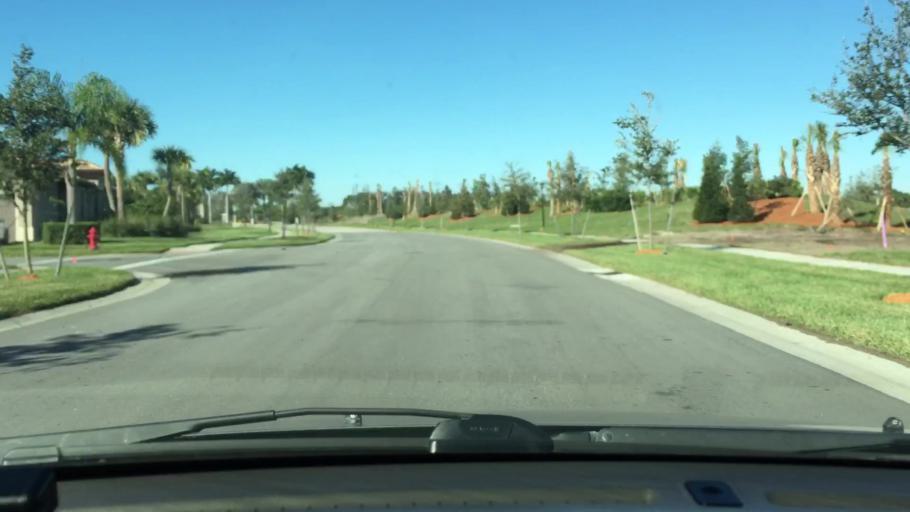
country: US
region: Florida
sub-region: Indian River County
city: Gifford
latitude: 27.6895
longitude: -80.4322
